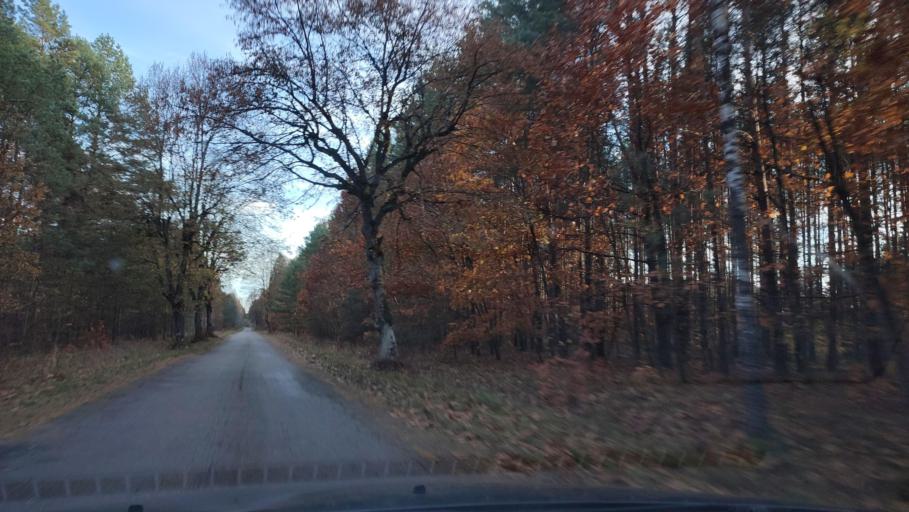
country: PL
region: Warmian-Masurian Voivodeship
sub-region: Powiat szczycienski
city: Jedwabno
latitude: 53.3633
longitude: 20.7312
